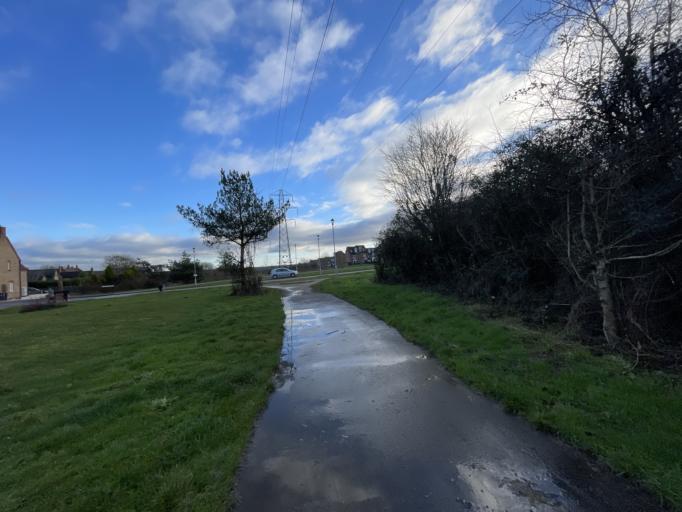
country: GB
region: England
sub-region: Warwickshire
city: Rugby
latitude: 52.3994
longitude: -1.2378
